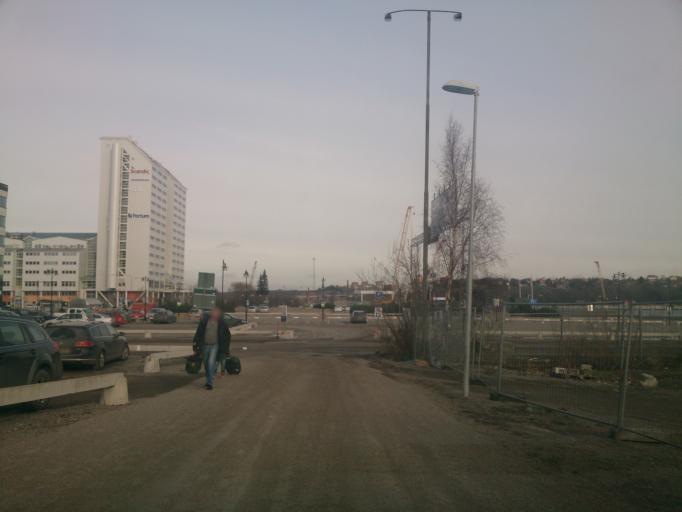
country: SE
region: Stockholm
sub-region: Lidingo
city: Lidingoe
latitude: 59.3468
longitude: 18.1143
